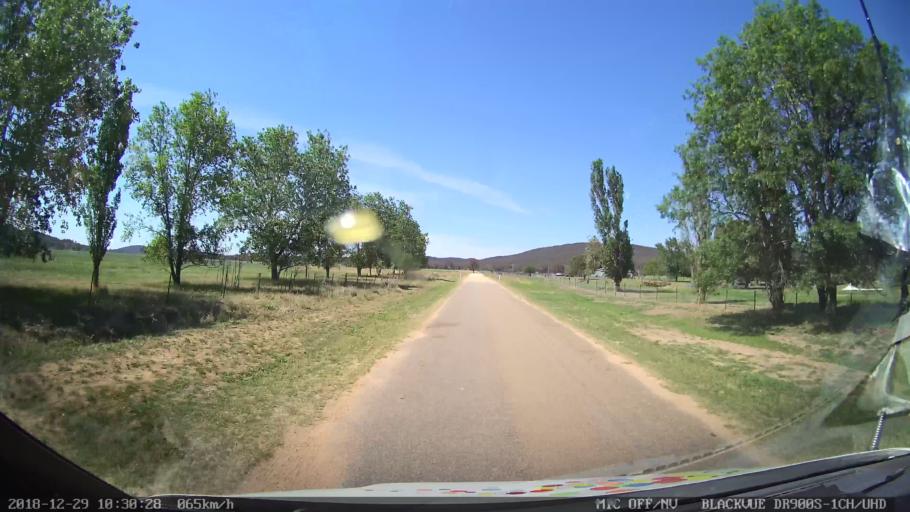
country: AU
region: New South Wales
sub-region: Yass Valley
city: Gundaroo
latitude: -34.9610
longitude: 149.4546
